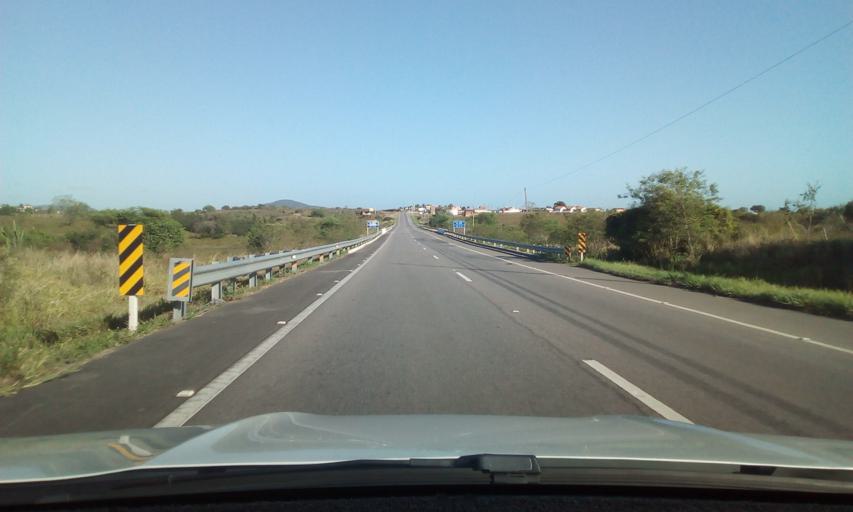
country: BR
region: Paraiba
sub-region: Gurinhem
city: Gurinhem
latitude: -7.1724
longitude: -35.3288
